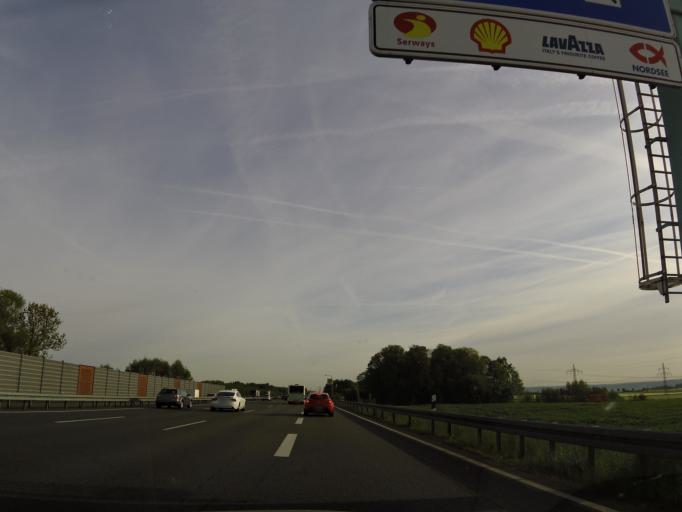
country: DE
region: Lower Saxony
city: Rosdorf
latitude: 51.4848
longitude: 9.8754
